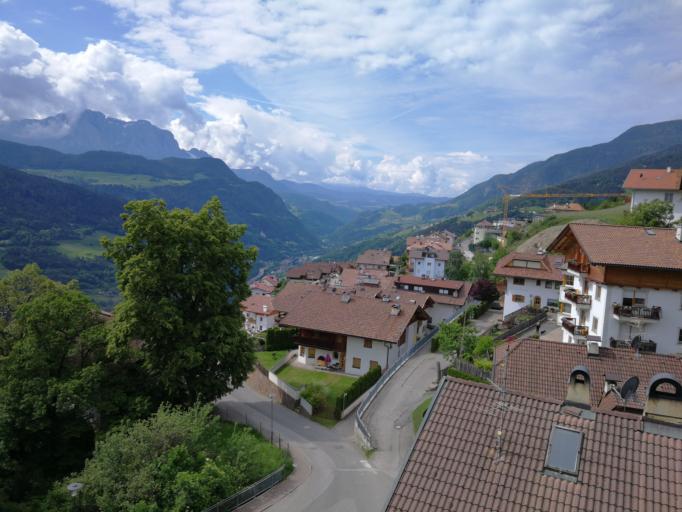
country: IT
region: Trentino-Alto Adige
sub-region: Bolzano
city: Villandro
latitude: 46.6308
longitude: 11.5380
